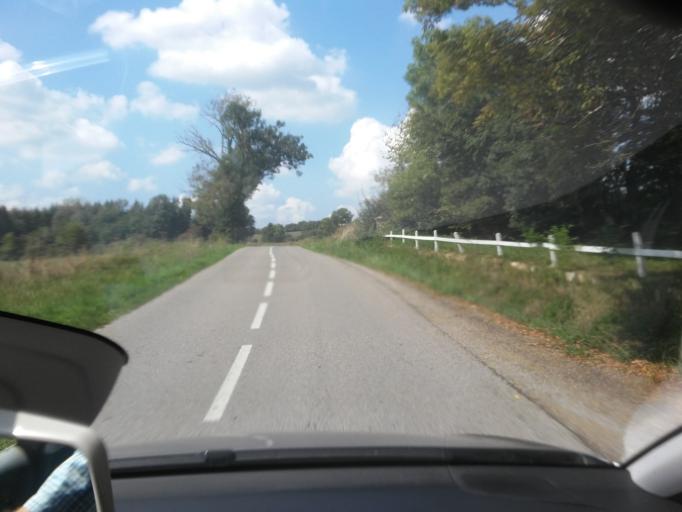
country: BE
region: Wallonia
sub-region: Province du Luxembourg
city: Rouvroy
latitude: 49.4990
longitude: 5.4869
